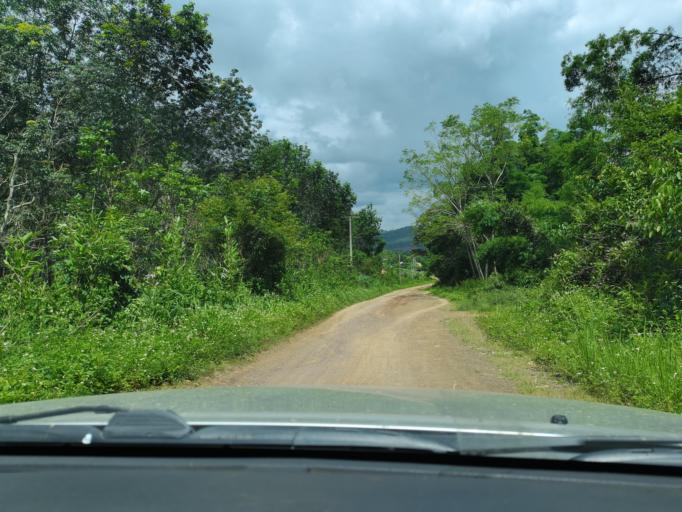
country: LA
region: Loungnamtha
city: Muang Long
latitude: 20.6842
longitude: 101.0478
